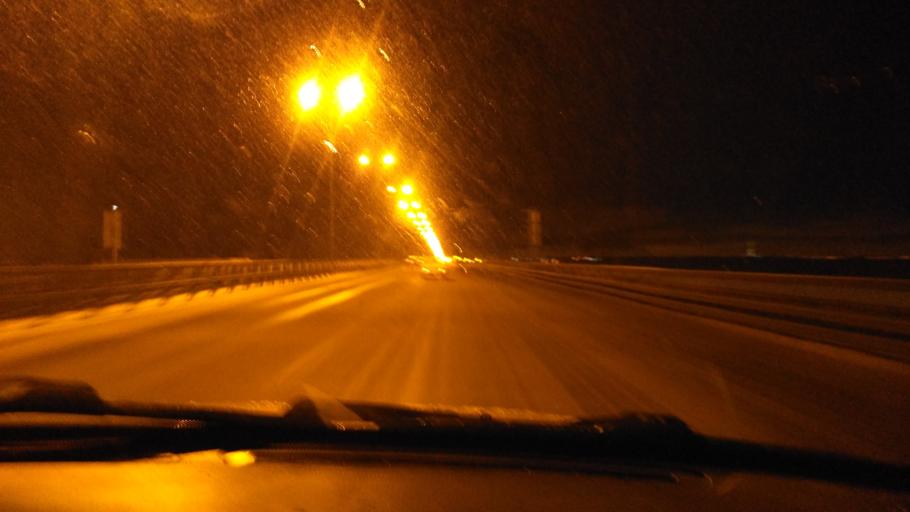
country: RU
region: St.-Petersburg
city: Kronshtadt
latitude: 60.0257
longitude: 29.8330
